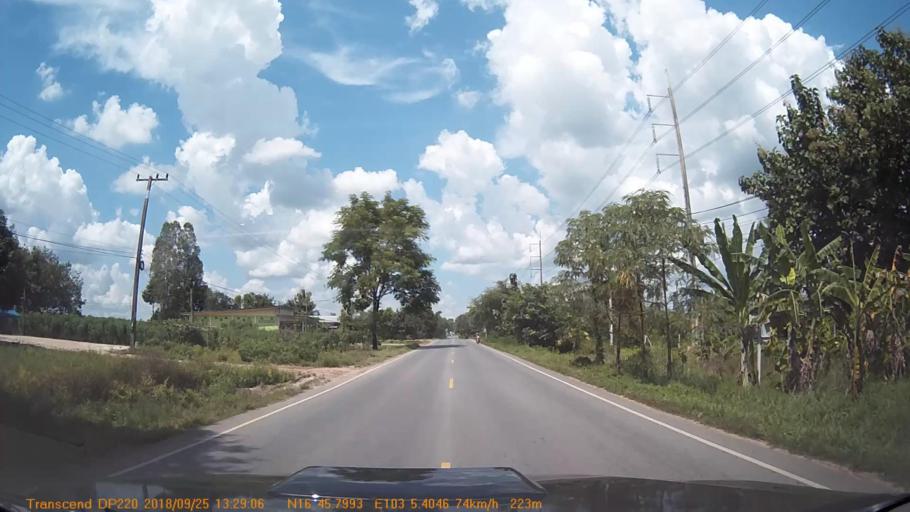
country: TH
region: Khon Kaen
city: Kranuan
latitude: 16.7633
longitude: 103.0901
